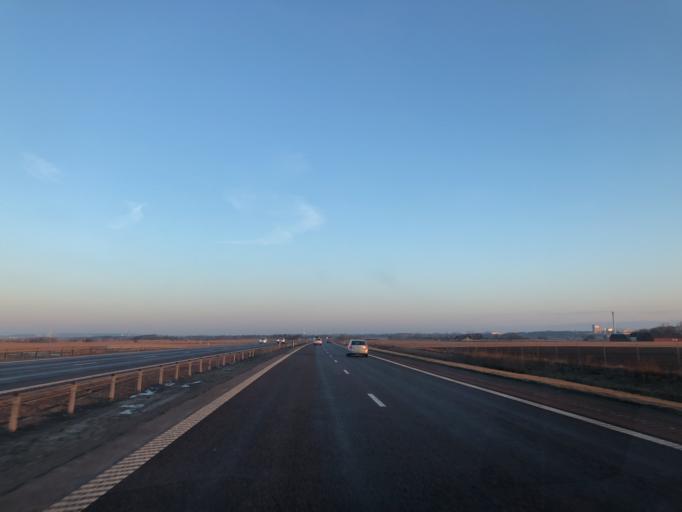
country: SE
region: Halland
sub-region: Halmstads Kommun
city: Troenninge
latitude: 56.6148
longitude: 12.9169
